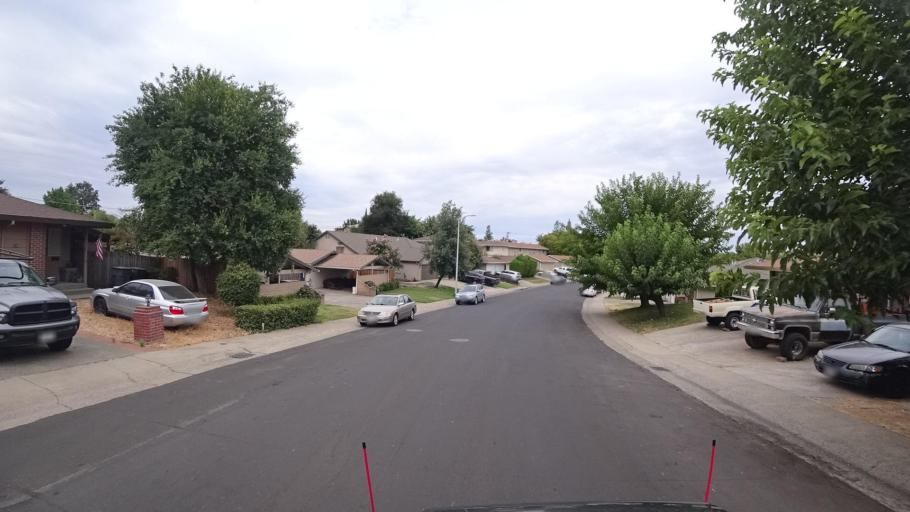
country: US
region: California
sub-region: Placer County
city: Rocklin
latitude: 38.7778
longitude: -121.2439
